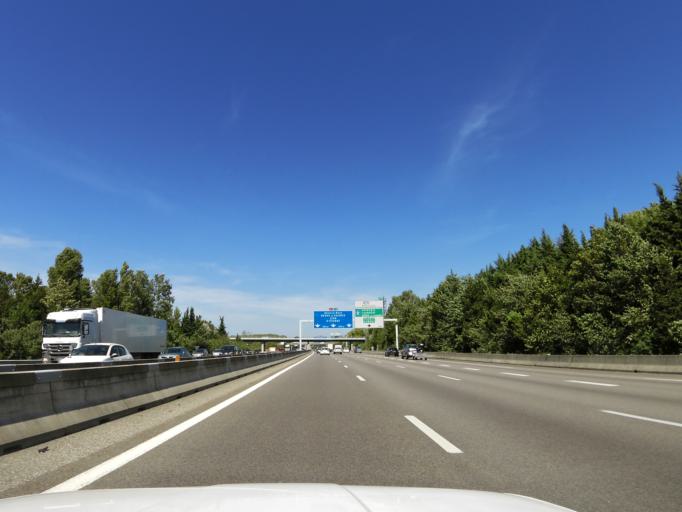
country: FR
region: Rhone-Alpes
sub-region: Departement de la Drome
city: Portes-les-Valence
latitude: 44.9000
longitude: 4.8750
